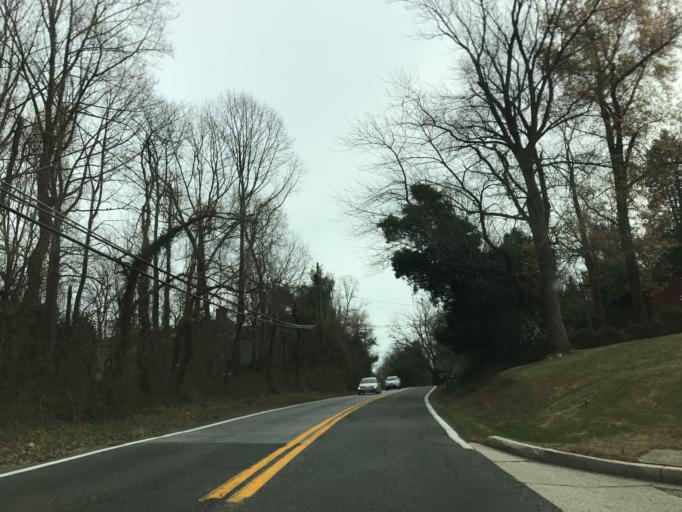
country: US
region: Maryland
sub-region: Anne Arundel County
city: Arnold
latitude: 39.0423
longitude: -76.5202
